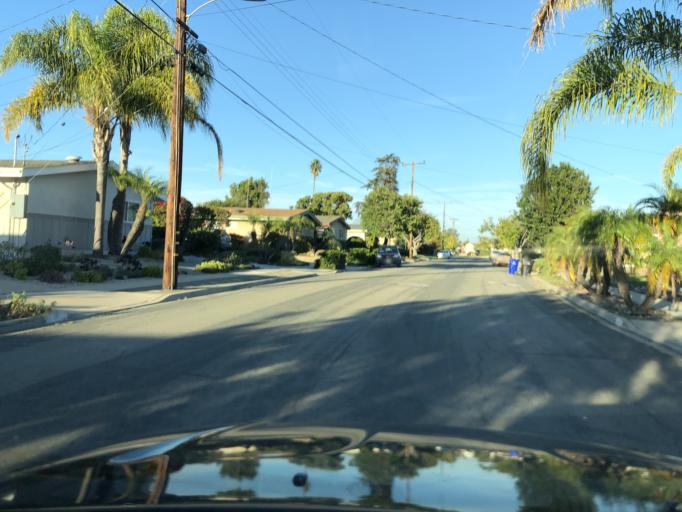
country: US
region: California
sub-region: San Diego County
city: La Jolla
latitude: 32.8169
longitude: -117.1956
